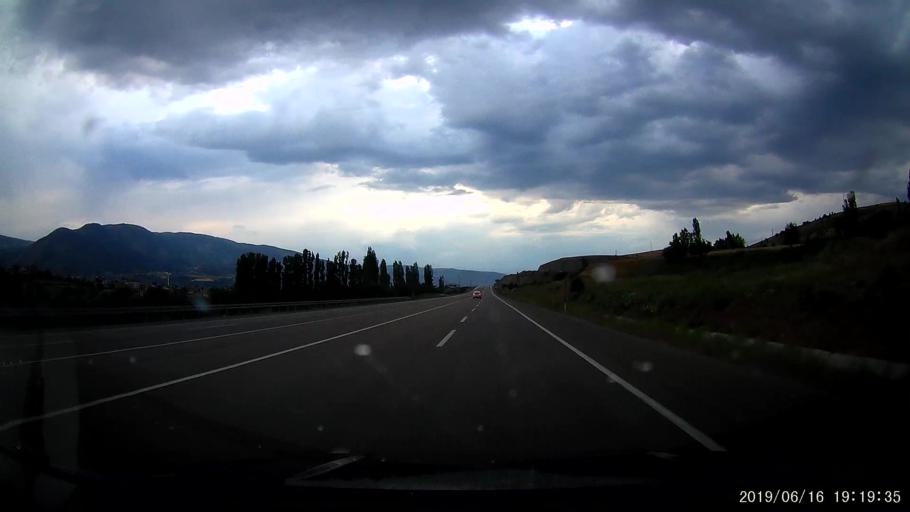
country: TR
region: Sivas
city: Akincilar
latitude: 40.0946
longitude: 38.4252
